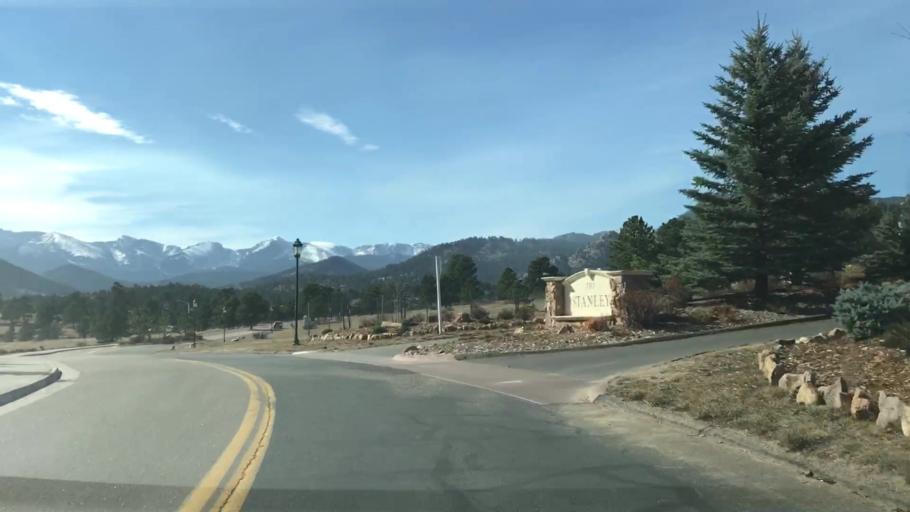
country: US
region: Colorado
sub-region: Larimer County
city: Estes Park
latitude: 40.3824
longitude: -105.5159
